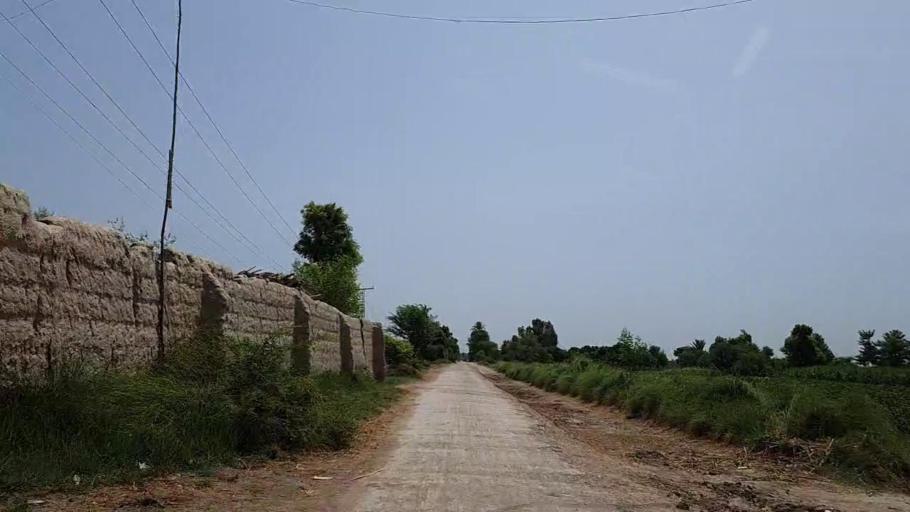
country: PK
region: Sindh
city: Naushahro Firoz
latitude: 26.8425
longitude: 67.9804
